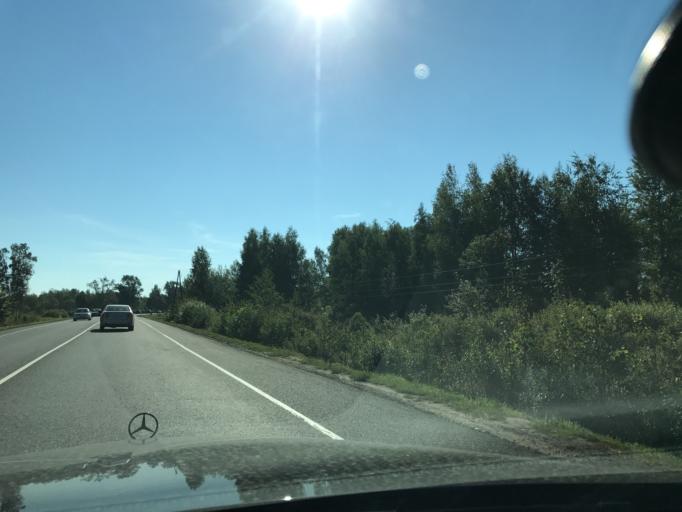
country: RU
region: Moskovskaya
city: Noginsk-9
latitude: 56.1035
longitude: 38.6434
